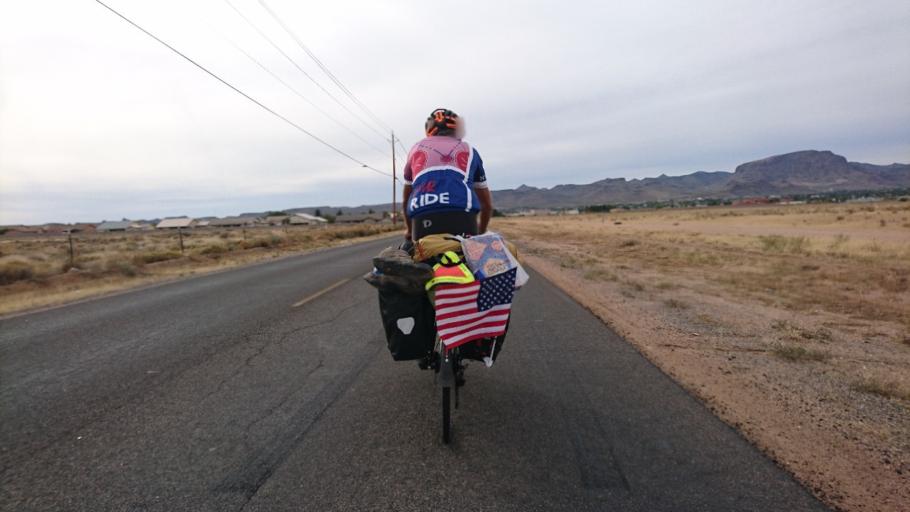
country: US
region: Arizona
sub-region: Mohave County
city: New Kingman-Butler
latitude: 35.2394
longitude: -113.9968
